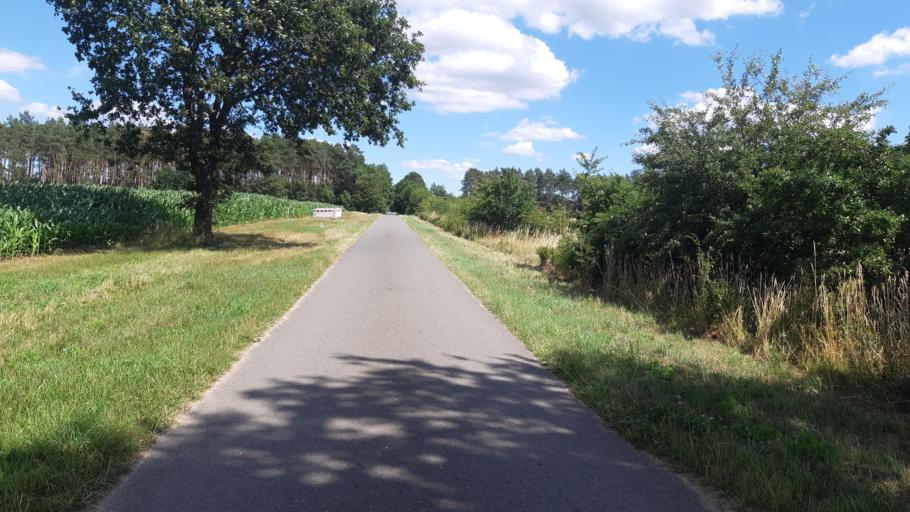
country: DE
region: Lower Saxony
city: Dahlem
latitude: 53.2053
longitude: 10.7837
